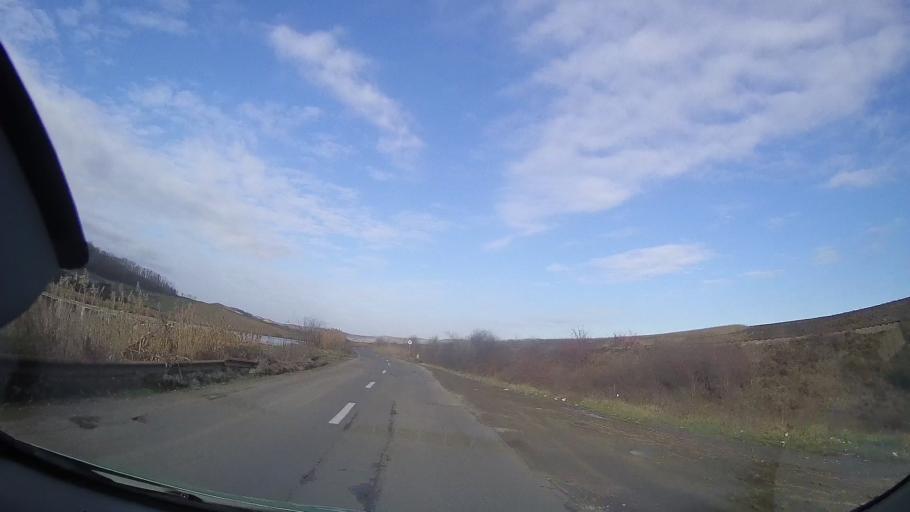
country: RO
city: Barza
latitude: 46.5563
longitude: 24.0999
